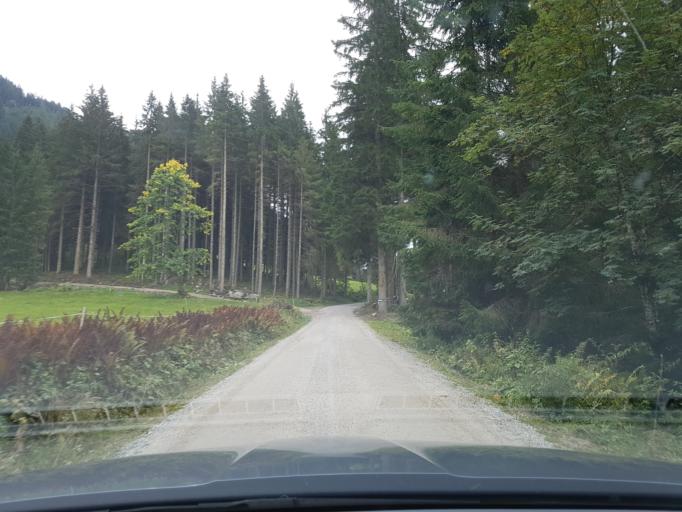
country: AT
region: Salzburg
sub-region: Politischer Bezirk Sankt Johann im Pongau
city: Forstau
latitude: 47.3451
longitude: 13.5752
